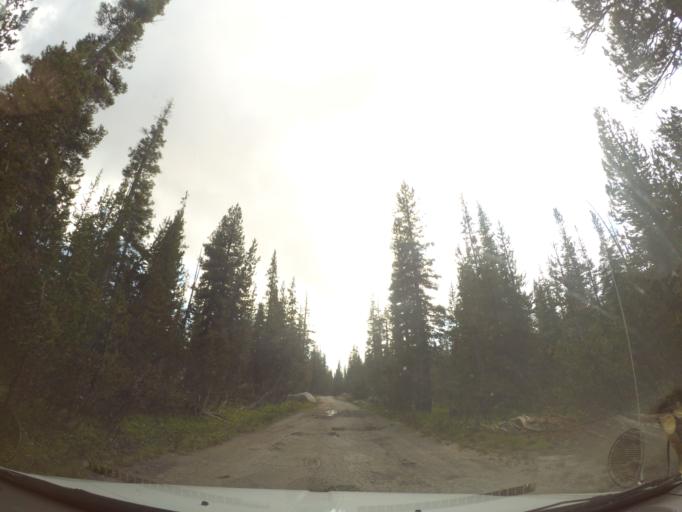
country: US
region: California
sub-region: Mariposa County
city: Yosemite Valley
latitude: 37.8295
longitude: -119.4996
